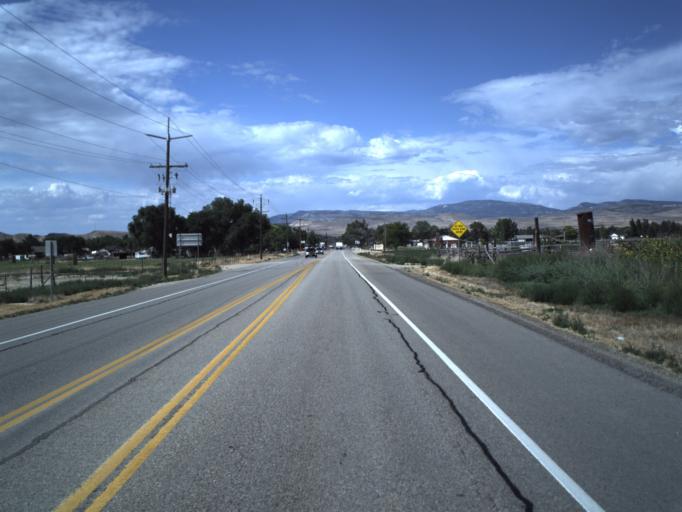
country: US
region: Utah
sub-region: Sanpete County
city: Centerfield
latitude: 39.1143
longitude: -111.8195
